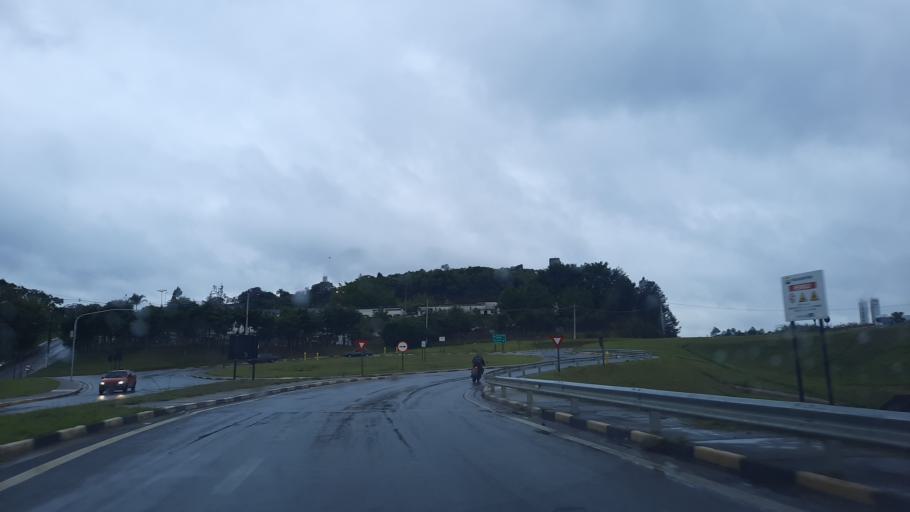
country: BR
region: Sao Paulo
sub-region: Atibaia
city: Atibaia
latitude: -23.0981
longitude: -46.5503
